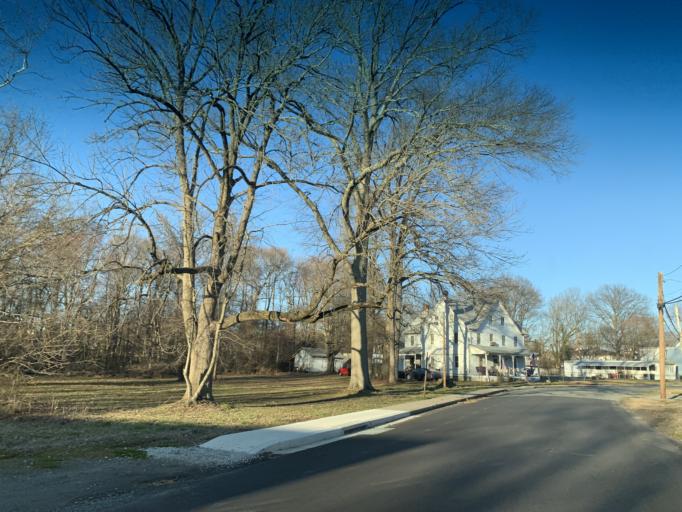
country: US
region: Maryland
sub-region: Cecil County
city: Perryville
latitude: 39.5613
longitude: -76.0737
